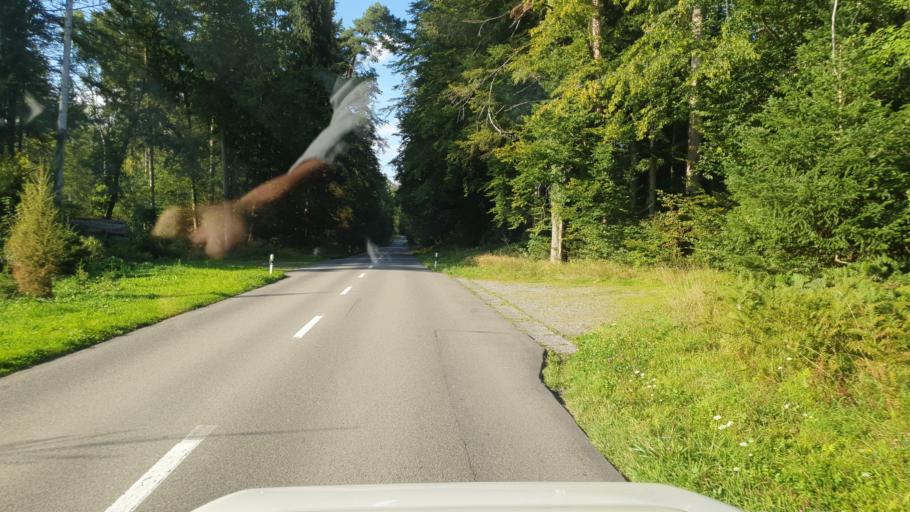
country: CH
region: Aargau
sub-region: Bezirk Muri
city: Waltenschwil
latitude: 47.3228
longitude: 8.3289
